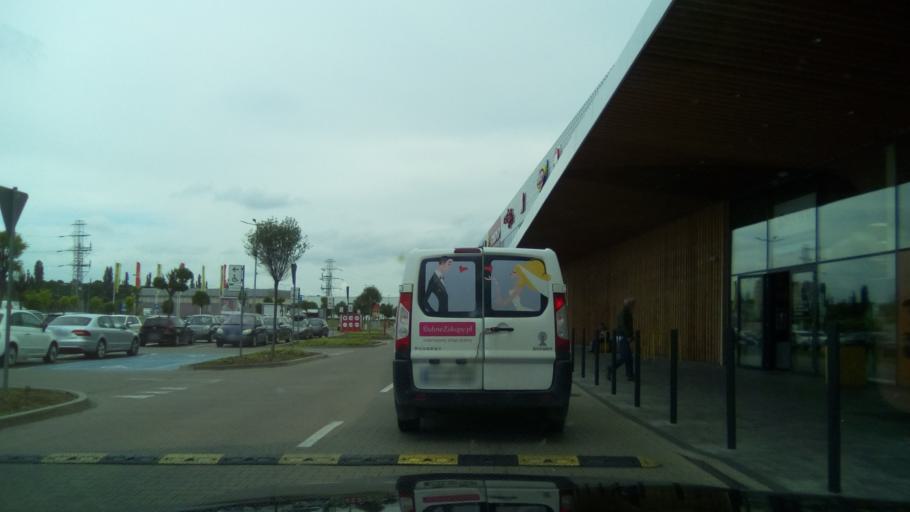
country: PL
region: Greater Poland Voivodeship
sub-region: Poznan
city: Poznan
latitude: 52.3795
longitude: 16.9828
